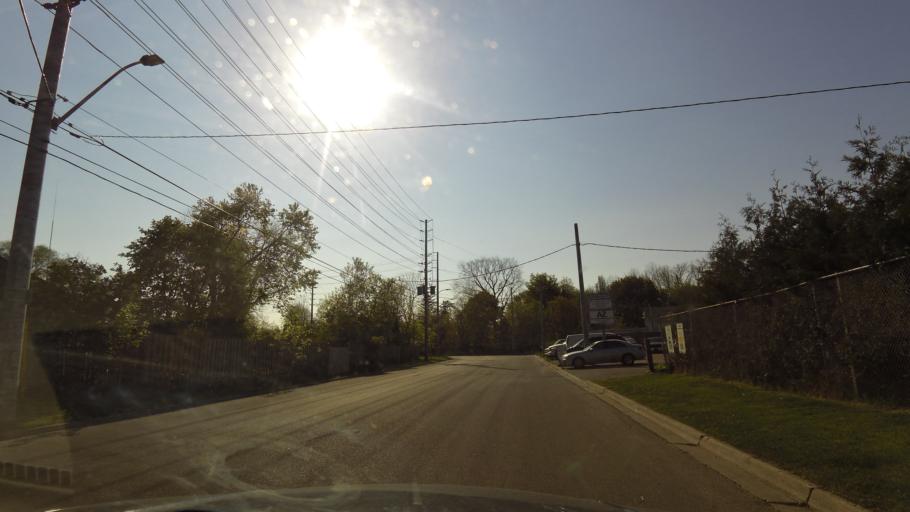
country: CA
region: Ontario
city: Mississauga
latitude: 43.5636
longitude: -79.5773
